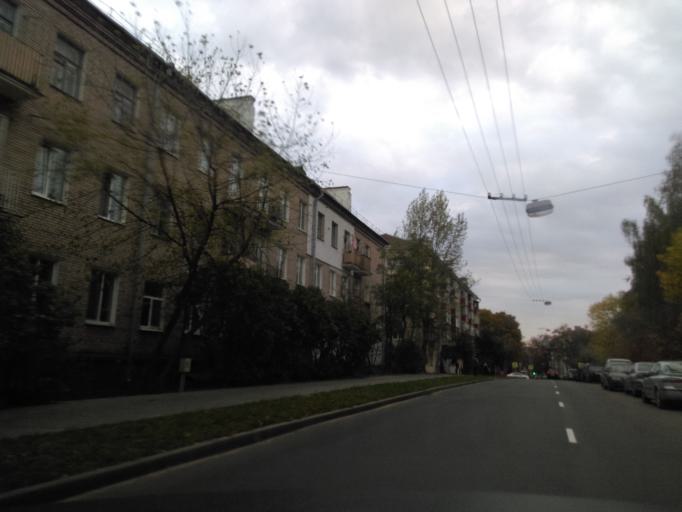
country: BY
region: Minsk
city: Minsk
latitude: 53.9119
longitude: 27.5844
